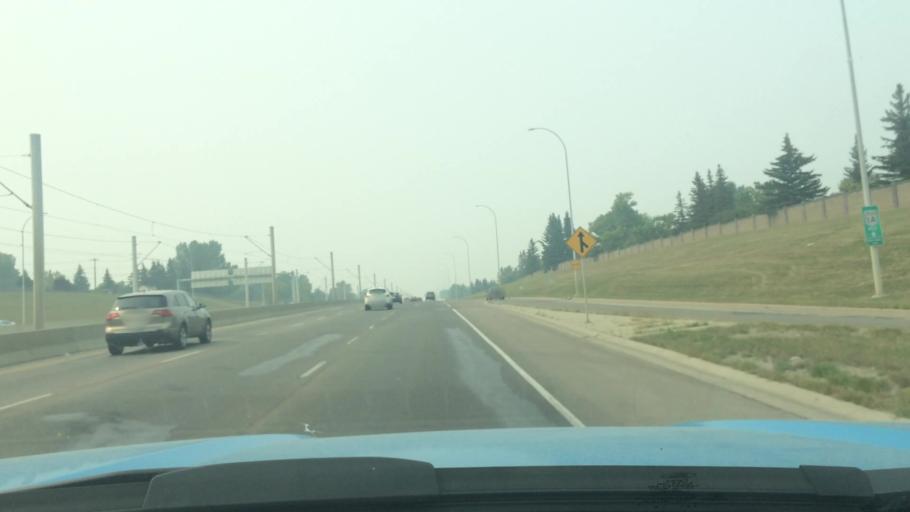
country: CA
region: Alberta
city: Calgary
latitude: 51.1121
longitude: -114.1813
